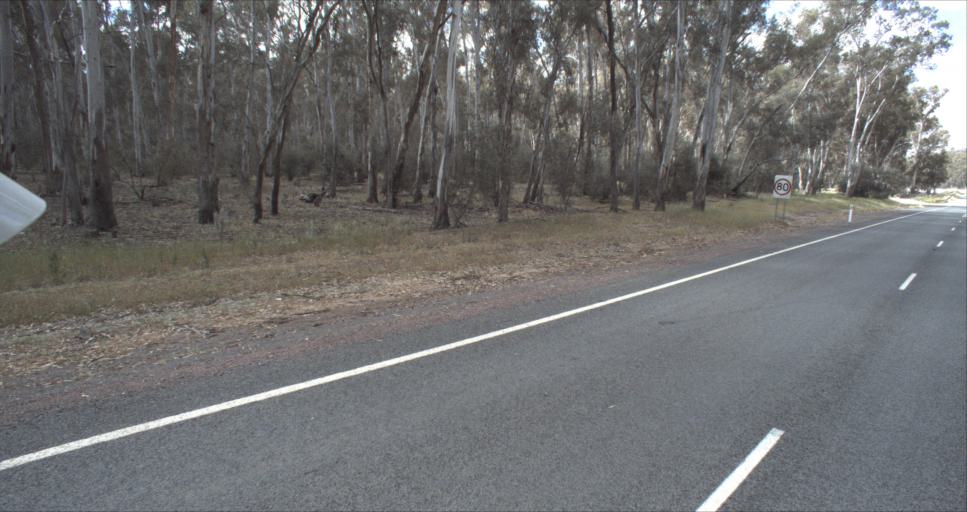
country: AU
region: New South Wales
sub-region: Leeton
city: Leeton
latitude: -34.6402
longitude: 146.3708
